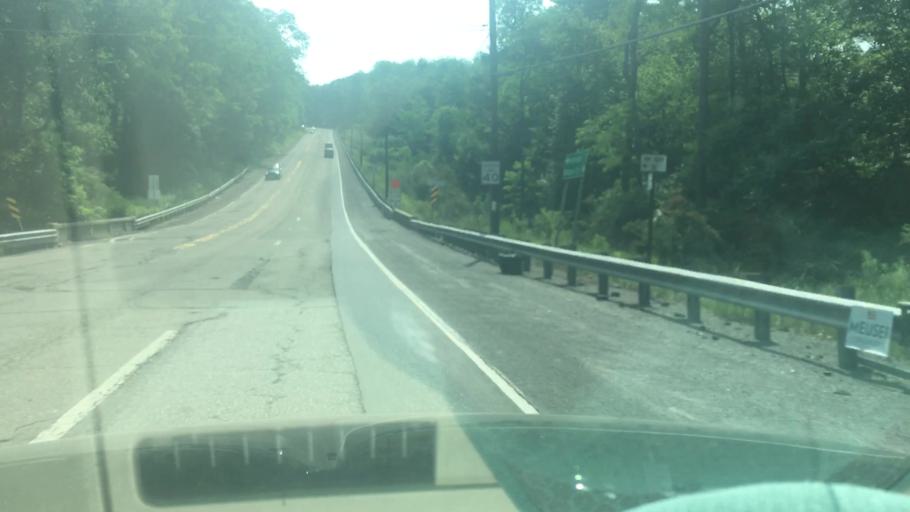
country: US
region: Pennsylvania
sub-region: Schuylkill County
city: Hometown
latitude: 40.8217
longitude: -76.0040
